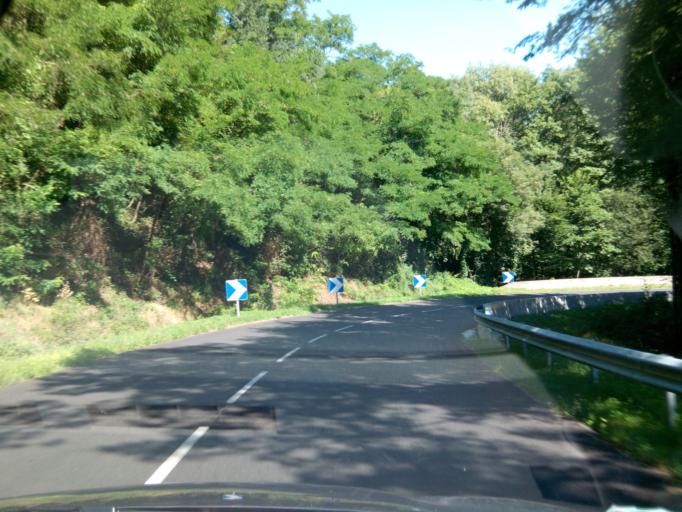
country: FR
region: Limousin
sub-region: Departement de la Correze
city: Beynat
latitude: 45.1239
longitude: 1.7175
